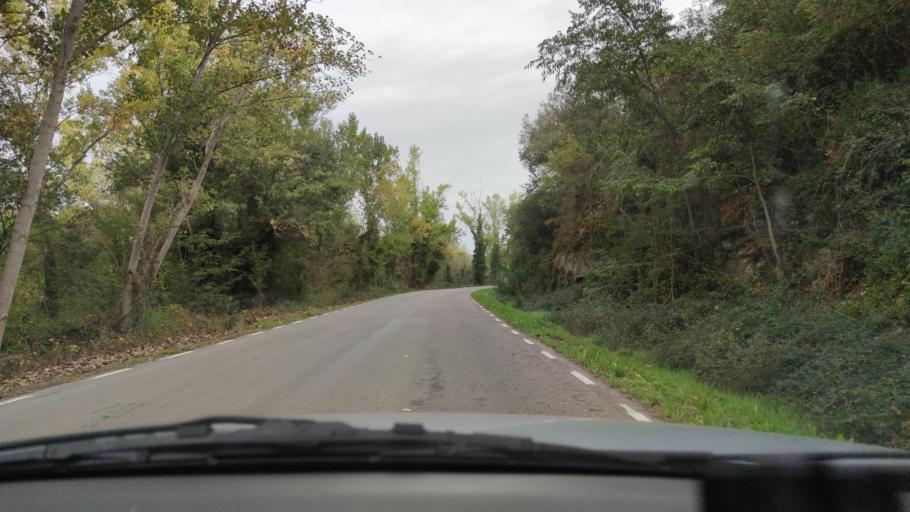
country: ES
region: Catalonia
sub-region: Provincia de Lleida
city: Artesa de Segre
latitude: 41.9156
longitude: 1.0778
